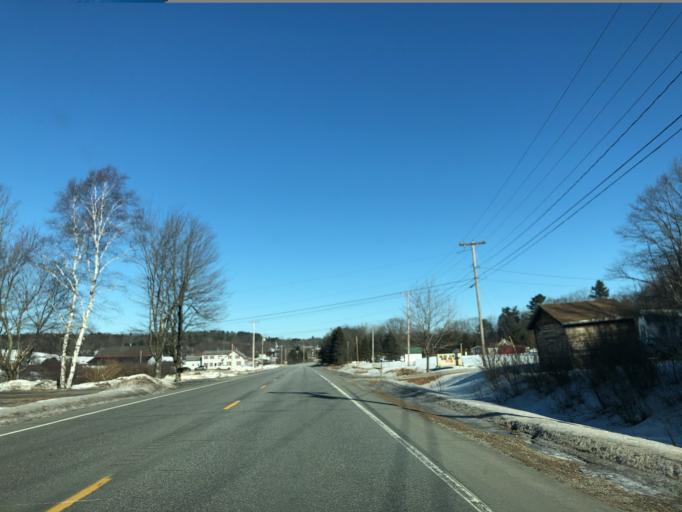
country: US
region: Maine
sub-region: Cumberland County
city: New Gloucester
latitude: 44.0114
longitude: -70.2872
